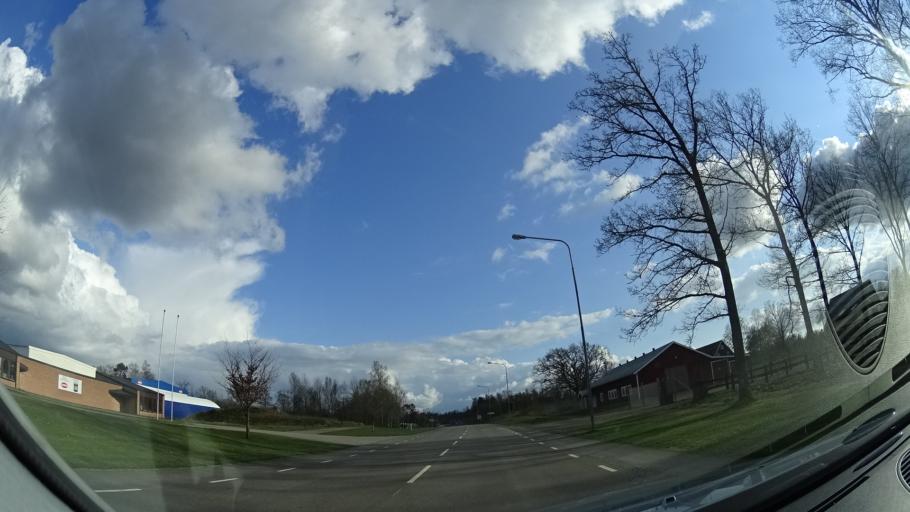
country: SE
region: Skane
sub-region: Perstorps Kommun
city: Perstorp
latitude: 56.1381
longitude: 13.3760
